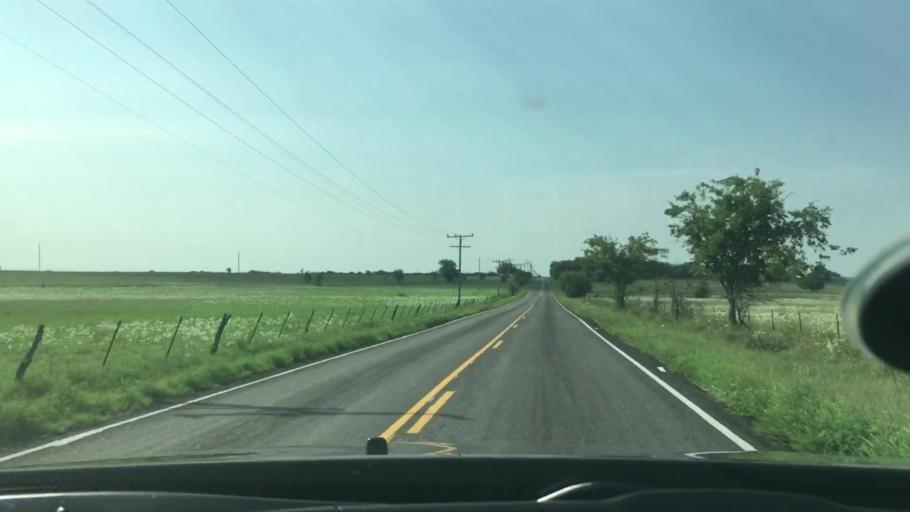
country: US
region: Oklahoma
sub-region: Bryan County
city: Durant
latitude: 34.1345
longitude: -96.4937
